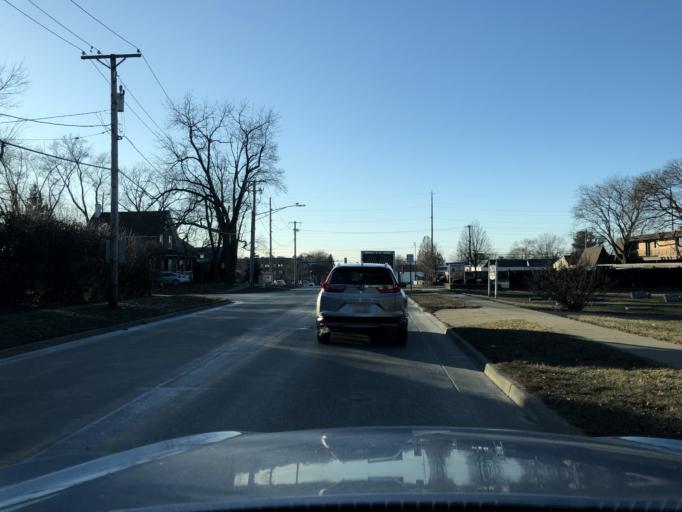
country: US
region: Illinois
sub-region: Cook County
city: Barrington
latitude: 42.1543
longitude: -88.1264
